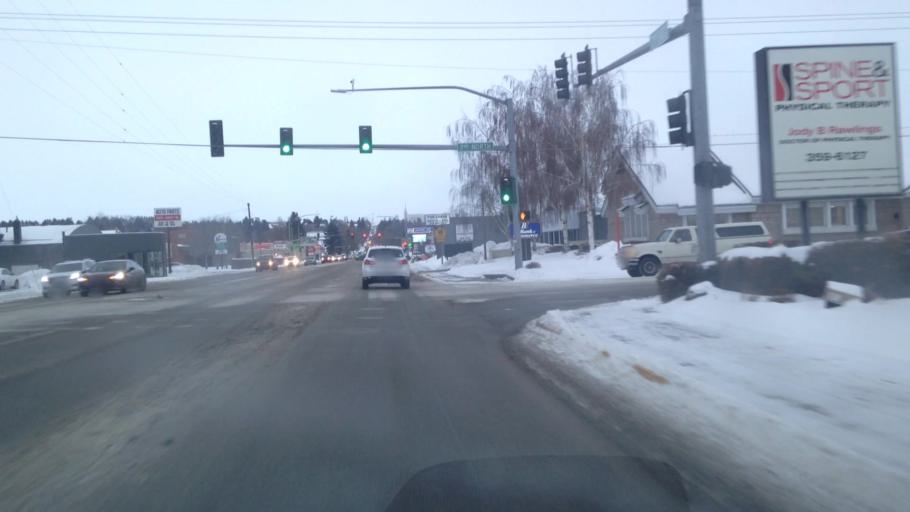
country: US
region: Idaho
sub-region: Madison County
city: Rexburg
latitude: 43.8305
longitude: -111.7782
